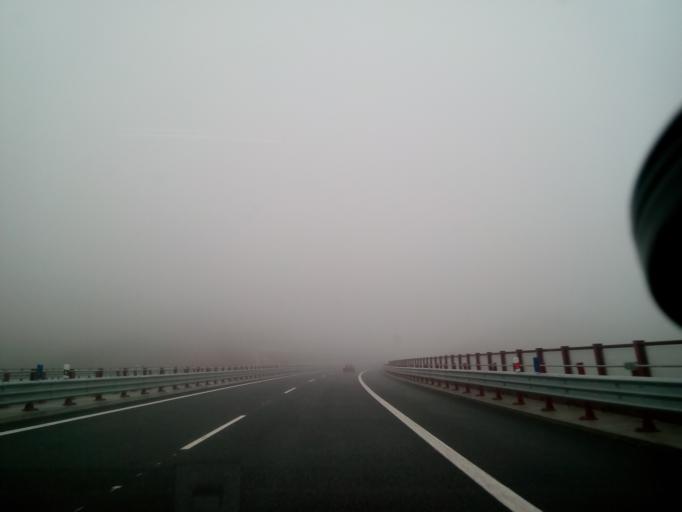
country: SK
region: Presovsky
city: Lipany
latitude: 49.0246
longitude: 20.9909
